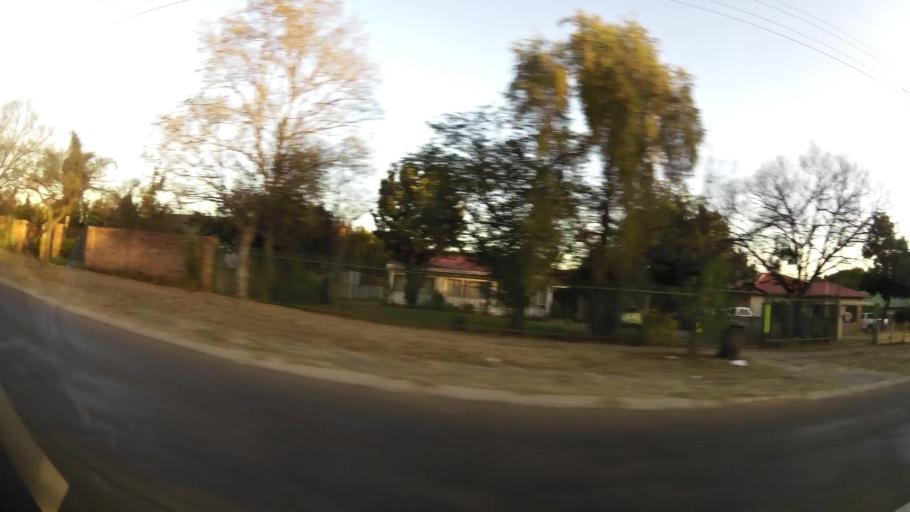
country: ZA
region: Gauteng
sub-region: City of Tshwane Metropolitan Municipality
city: Pretoria
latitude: -25.7115
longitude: 28.2442
